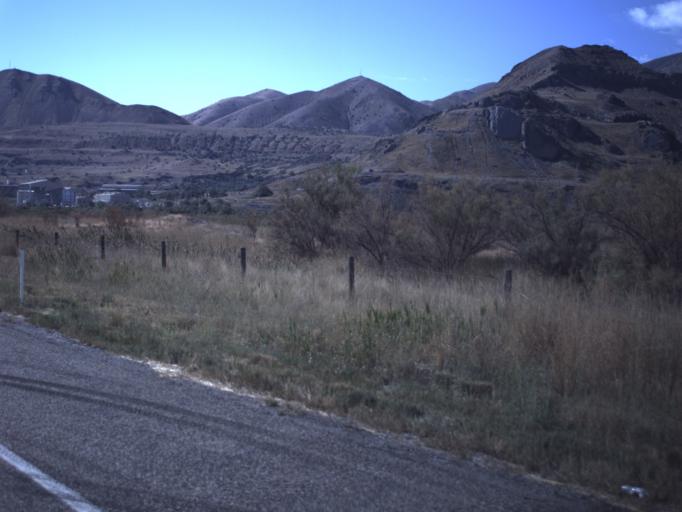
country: US
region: Utah
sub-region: Salt Lake County
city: Magna
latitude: 40.7382
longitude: -112.1748
